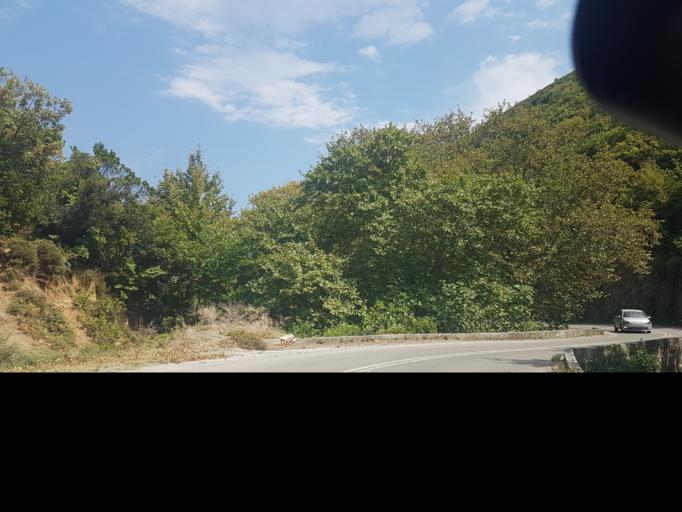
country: GR
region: Central Greece
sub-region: Nomos Evvoias
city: Kymi
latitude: 38.6393
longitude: 24.0830
